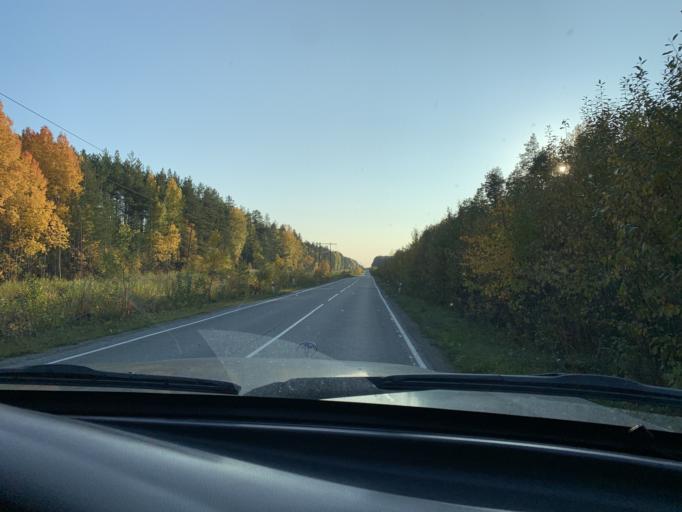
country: RU
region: Sverdlovsk
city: Verkhneye Dubrovo
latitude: 56.8769
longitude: 61.1148
